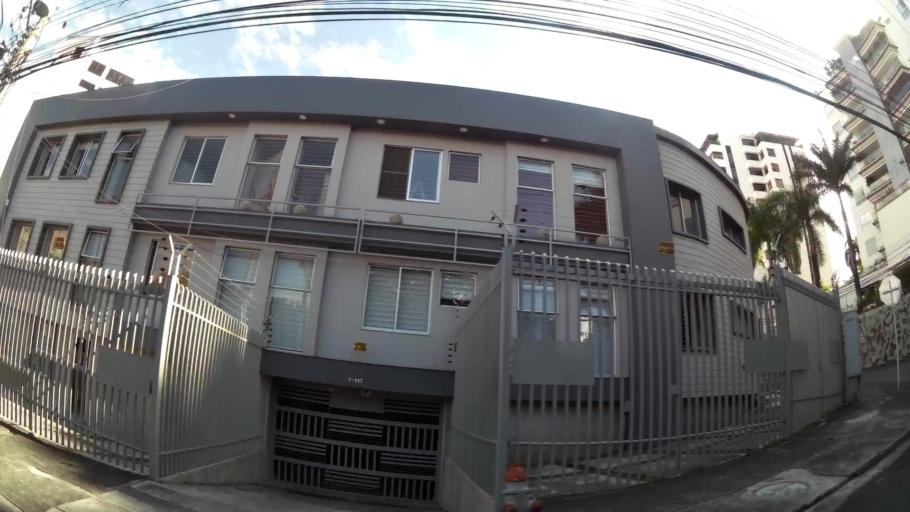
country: CO
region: Valle del Cauca
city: Cali
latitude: 3.4487
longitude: -76.5486
